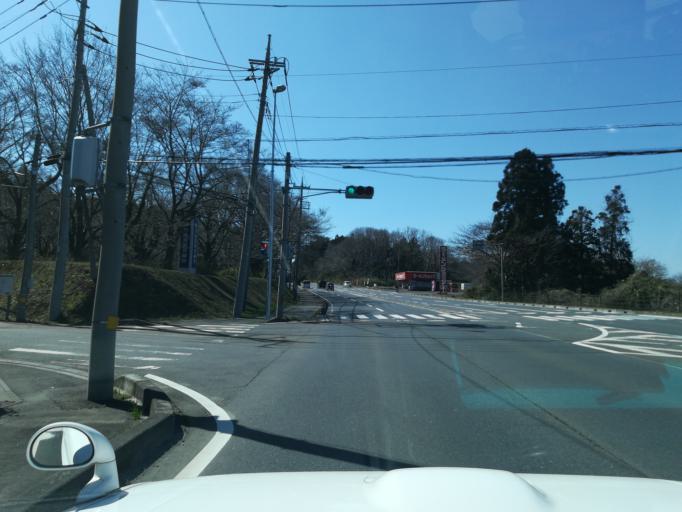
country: JP
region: Ibaraki
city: Ushiku
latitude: 35.9672
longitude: 140.1716
